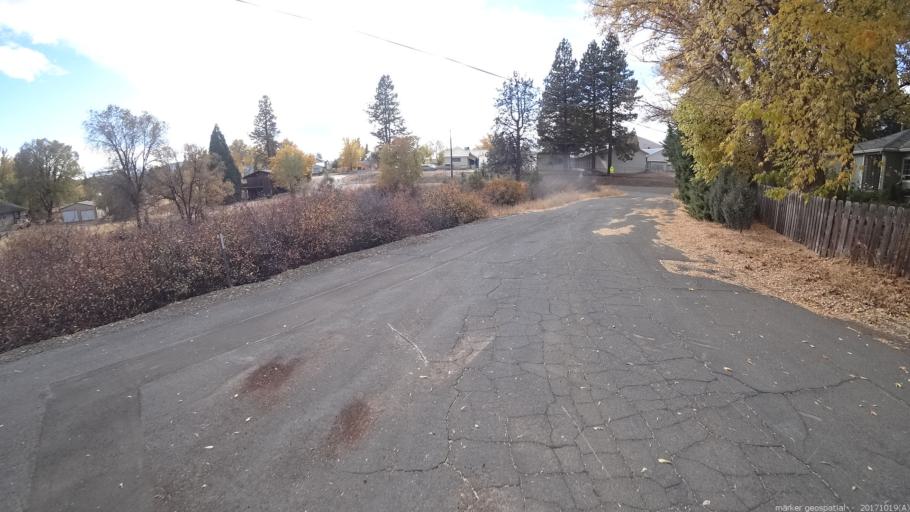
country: US
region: California
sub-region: Shasta County
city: Burney
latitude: 41.0067
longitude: -121.4390
